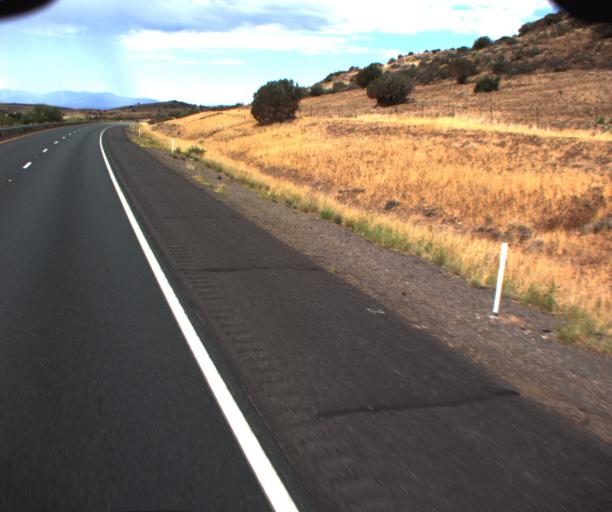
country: US
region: Arizona
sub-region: Yavapai County
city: Camp Verde
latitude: 34.4880
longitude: -112.0110
